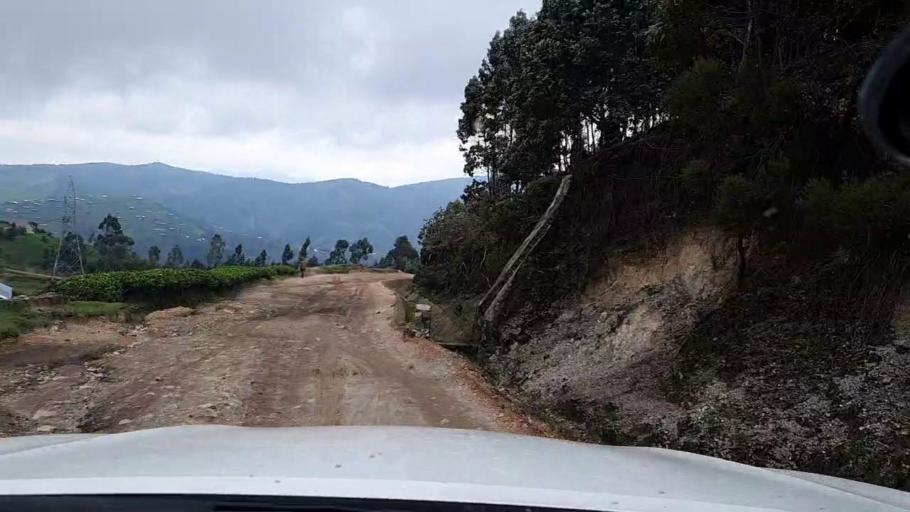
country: RW
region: Western Province
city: Kibuye
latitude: -2.2467
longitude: 29.3457
